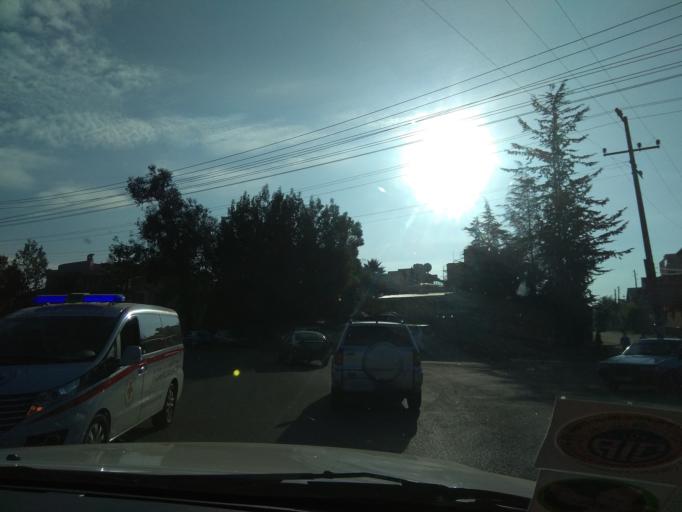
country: ET
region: Adis Abeba
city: Addis Ababa
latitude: 8.9897
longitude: 38.8016
